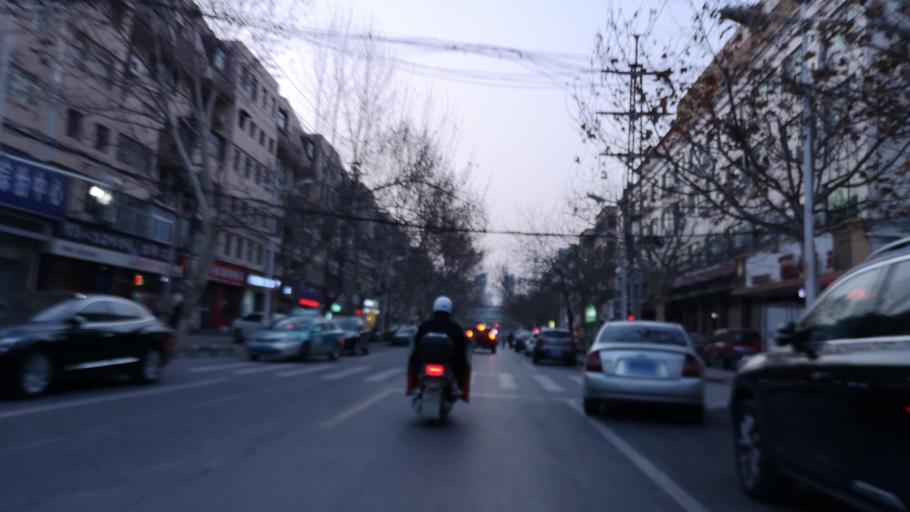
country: CN
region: Henan Sheng
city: Zhongyuanlu
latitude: 35.7660
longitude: 115.0666
